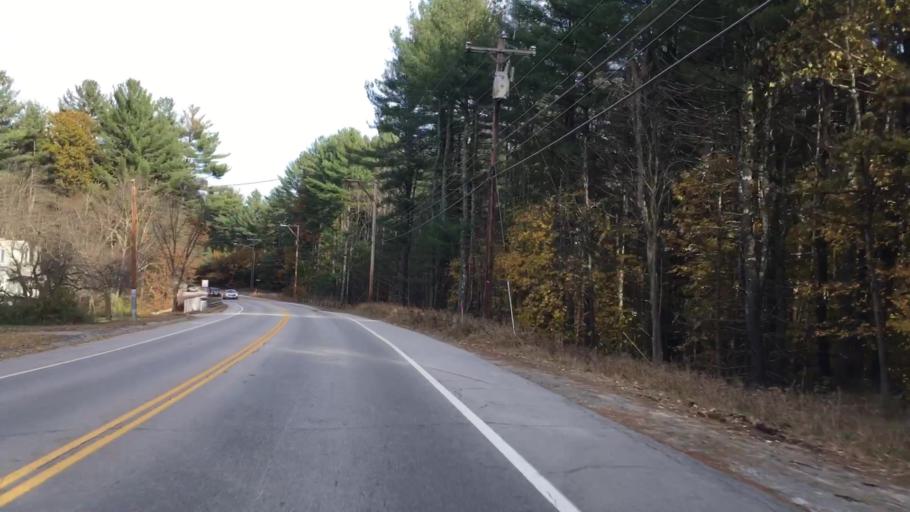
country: US
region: New Hampshire
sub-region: Hillsborough County
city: Milford
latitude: 42.8616
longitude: -71.6206
